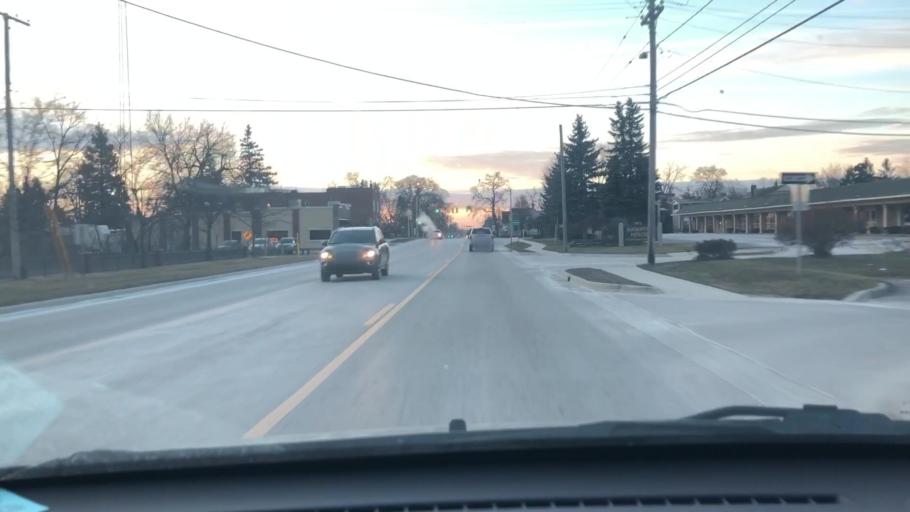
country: US
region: Michigan
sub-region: Macomb County
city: Shelby
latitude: 42.7260
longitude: -83.0360
